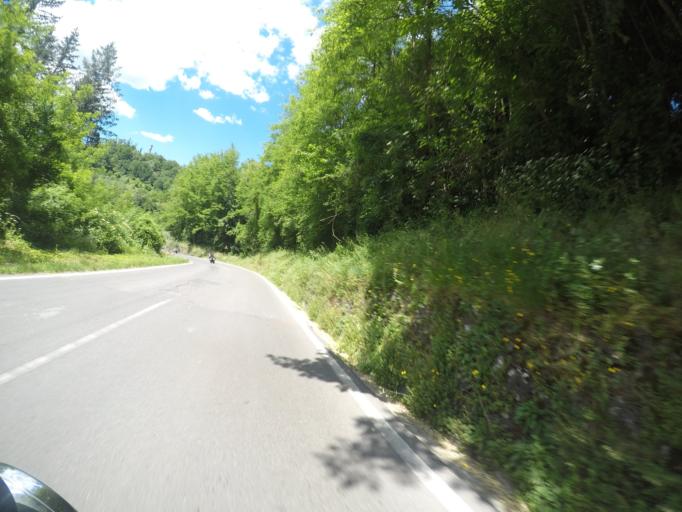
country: IT
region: Tuscany
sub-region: Provincia di Lucca
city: Pieve Fosciana
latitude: 44.1338
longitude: 10.3930
